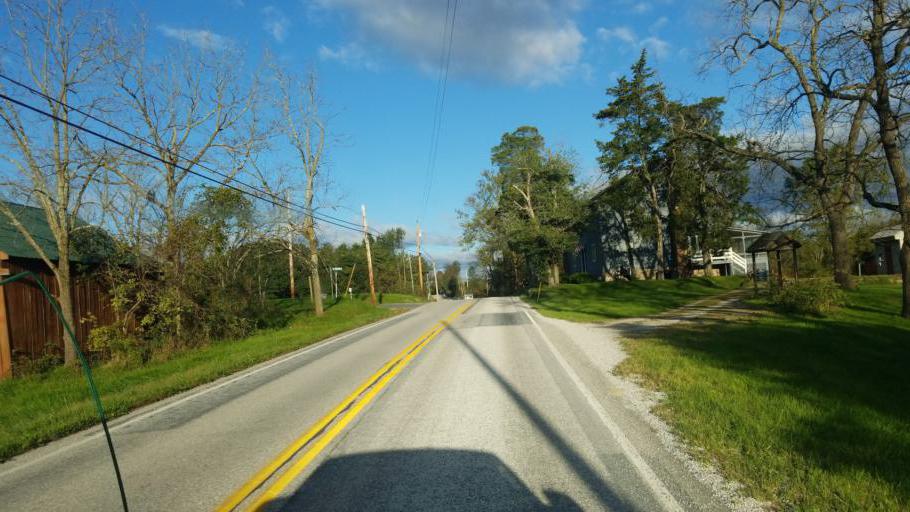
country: US
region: Pennsylvania
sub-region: Adams County
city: Biglerville
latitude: 39.8956
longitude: -77.1988
